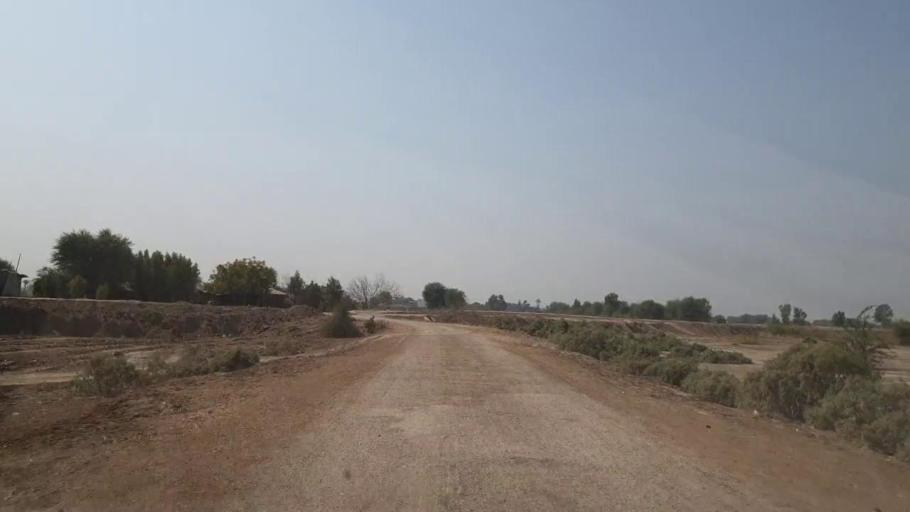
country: PK
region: Sindh
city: Mirpur Khas
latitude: 25.6358
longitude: 69.1426
